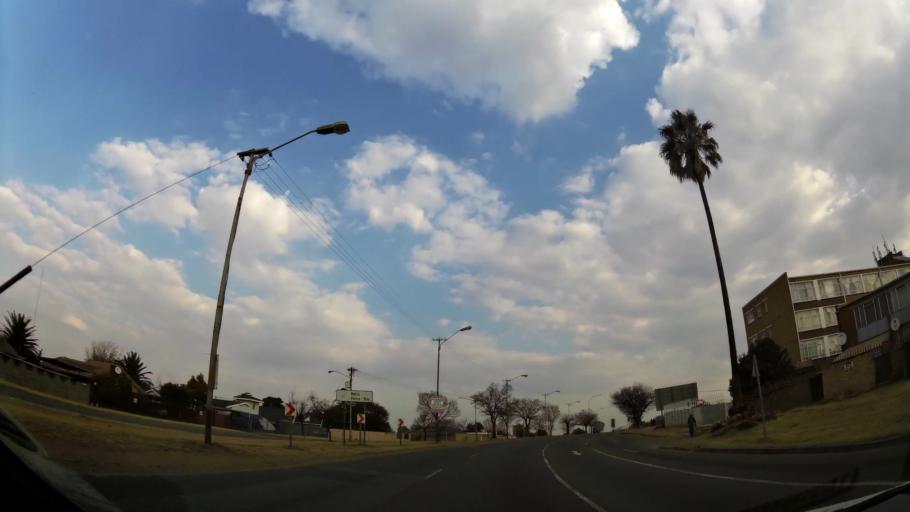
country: ZA
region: Gauteng
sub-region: Ekurhuleni Metropolitan Municipality
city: Germiston
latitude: -26.2383
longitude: 28.1957
